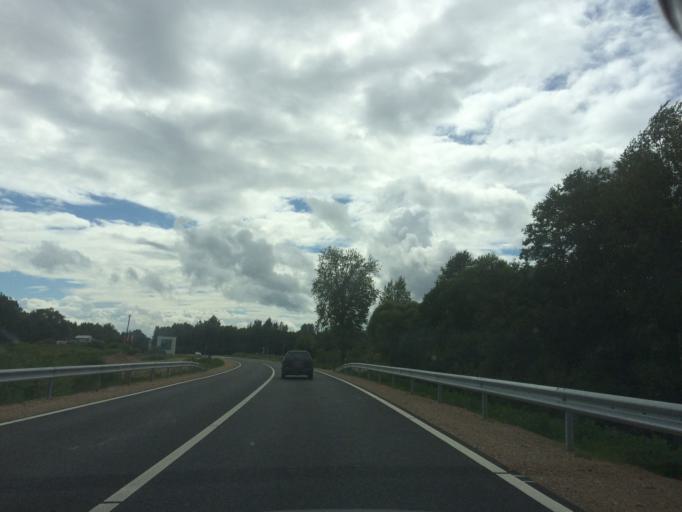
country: LV
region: Rezekne
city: Rezekne
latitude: 56.4913
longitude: 27.3156
